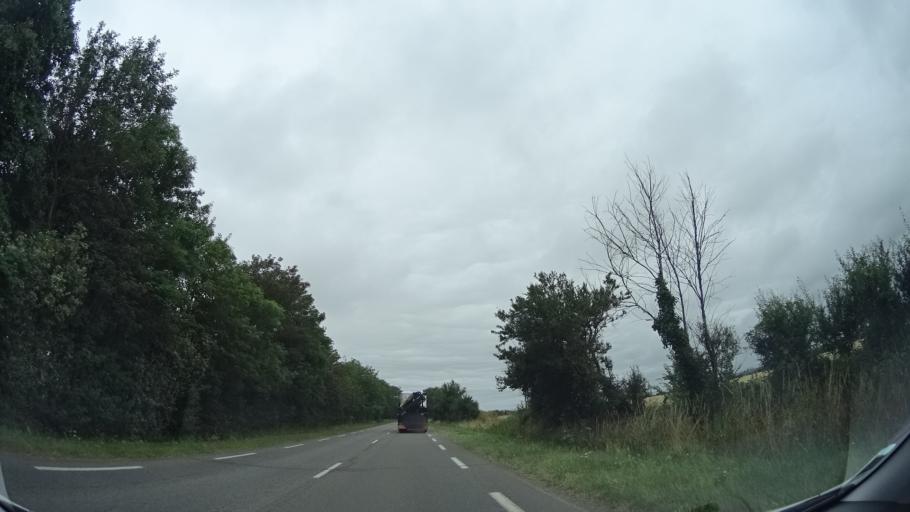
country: FR
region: Lower Normandy
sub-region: Departement de la Manche
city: Portbail
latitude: 49.3624
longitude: -1.7012
